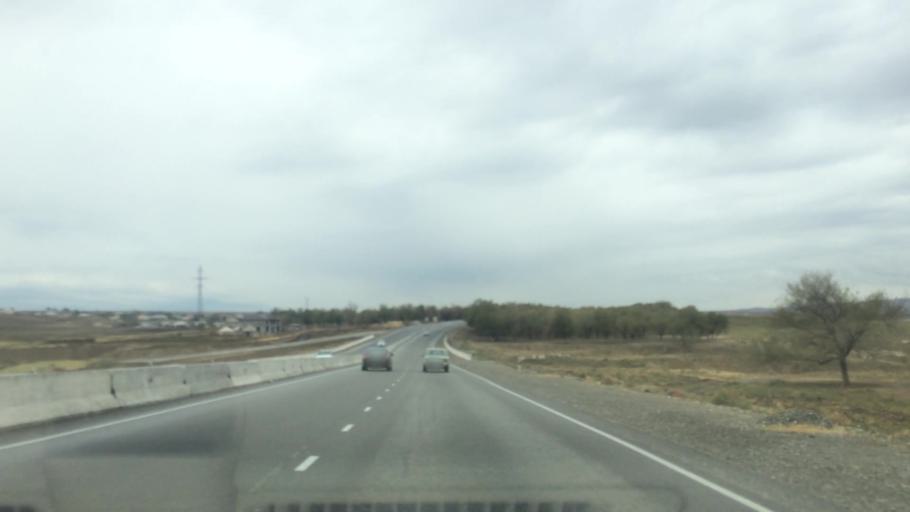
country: UZ
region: Samarqand
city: Bulung'ur
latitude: 39.9215
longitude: 67.5164
